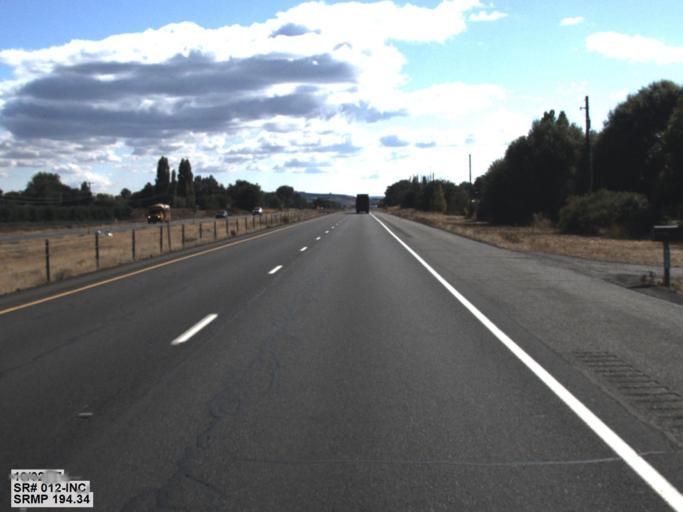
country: US
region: Washington
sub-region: Yakima County
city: Gleed
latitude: 46.6792
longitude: -120.6464
